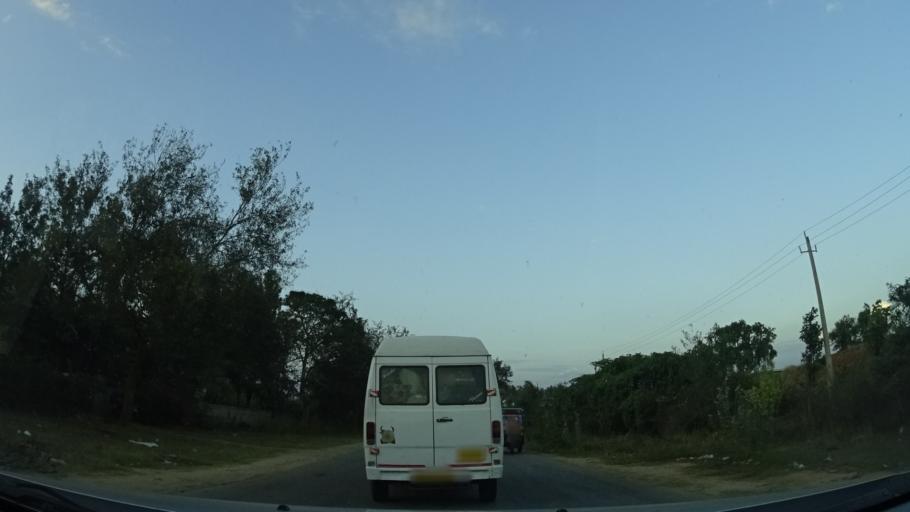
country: IN
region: Karnataka
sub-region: Ramanagara
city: Kanakapura
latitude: 12.6294
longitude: 77.4311
